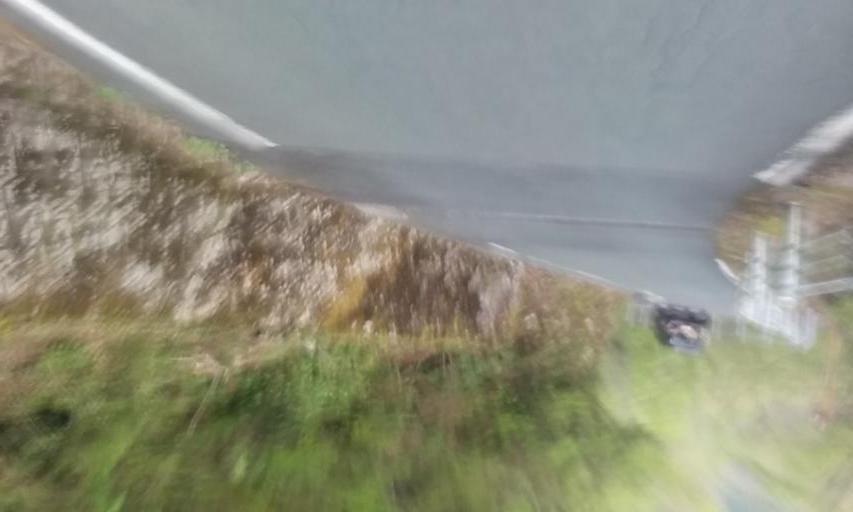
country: JP
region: Ehime
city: Saijo
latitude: 33.7955
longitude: 133.2686
